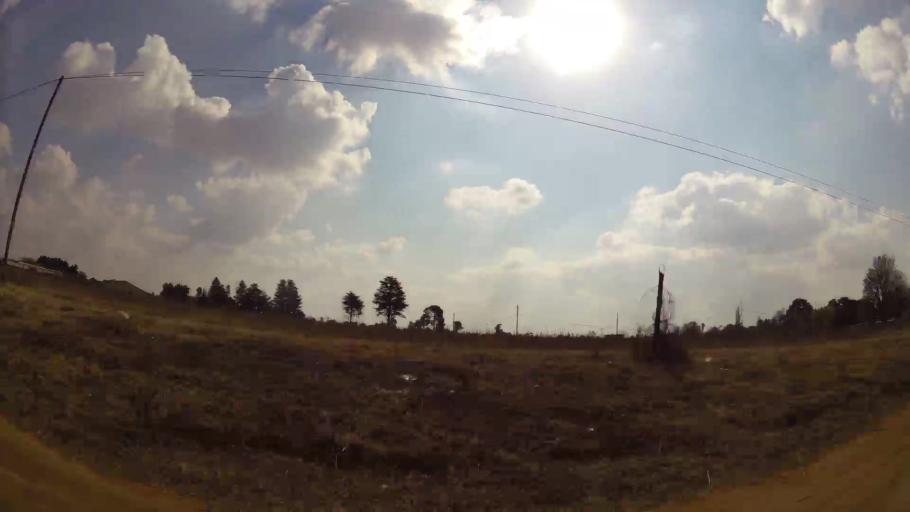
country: ZA
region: Mpumalanga
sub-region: Nkangala District Municipality
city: Delmas
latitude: -26.1605
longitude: 28.5497
